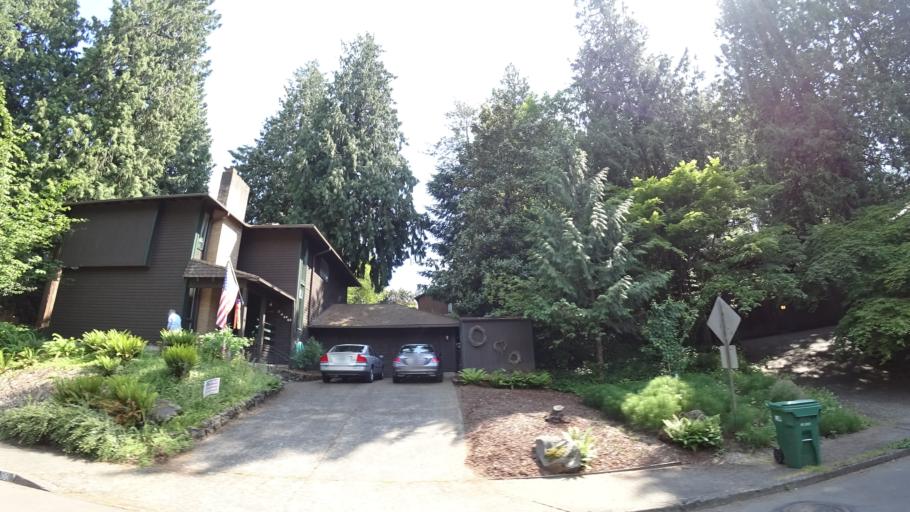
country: US
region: Oregon
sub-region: Washington County
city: Metzger
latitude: 45.4481
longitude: -122.7506
